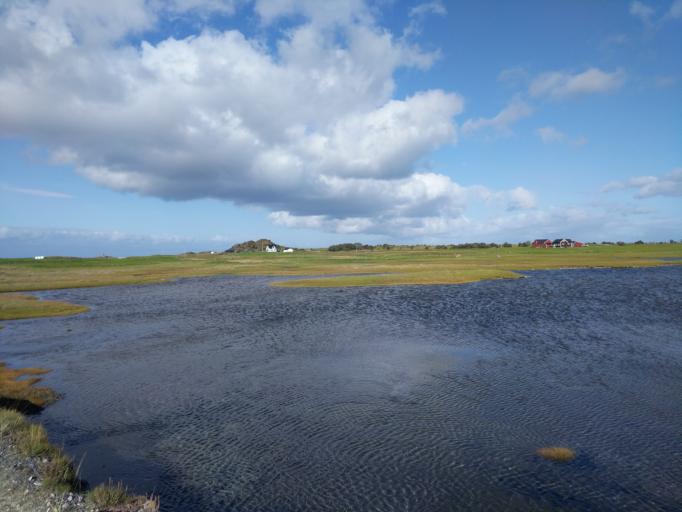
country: NO
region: Nordland
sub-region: Vestvagoy
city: Evjen
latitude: 68.3324
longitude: 13.8910
